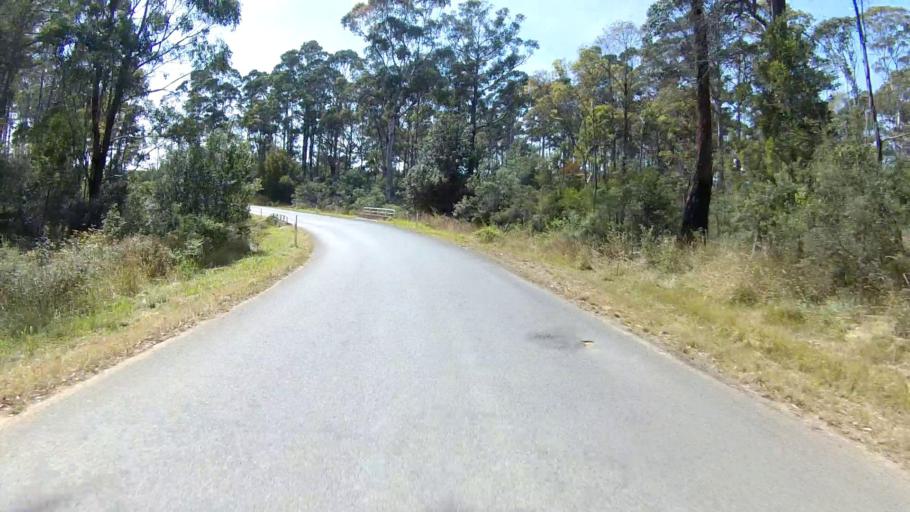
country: AU
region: Tasmania
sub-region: Sorell
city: Sorell
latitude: -42.7507
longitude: 147.7141
